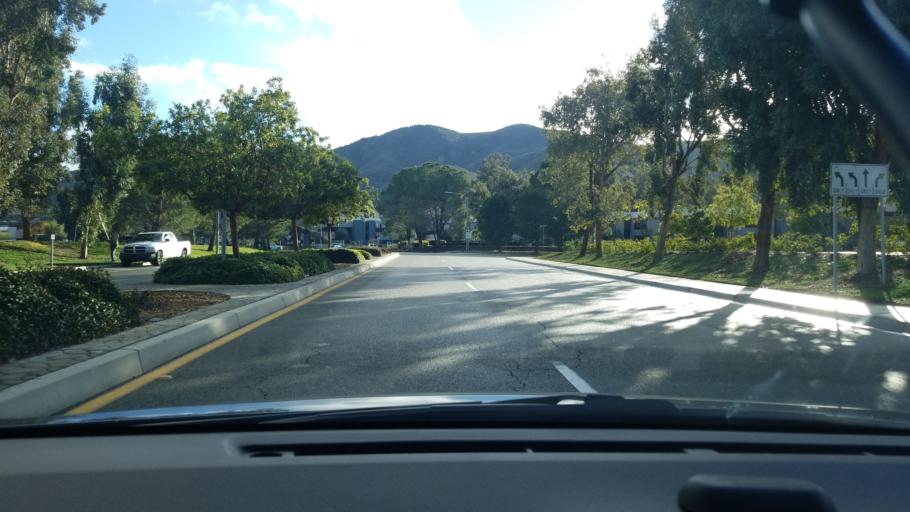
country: US
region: California
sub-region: Riverside County
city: Temecula
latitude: 33.4998
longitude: -117.1568
